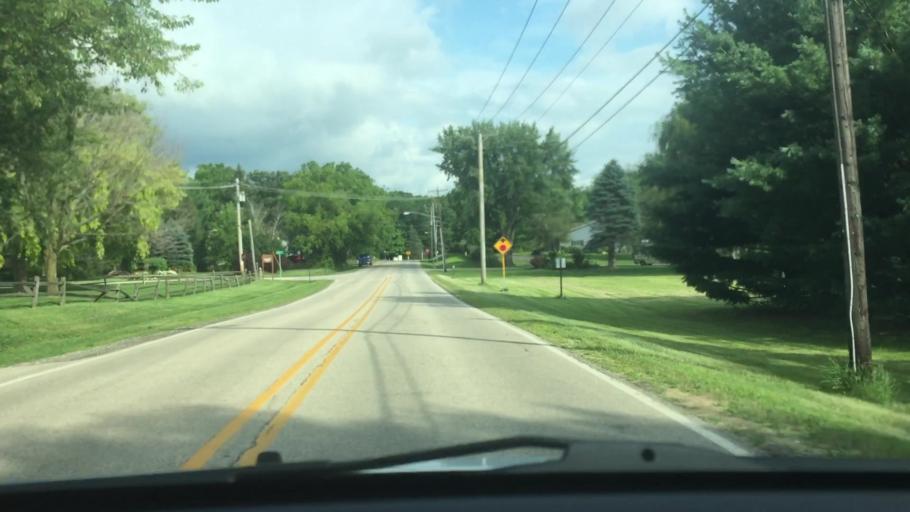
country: US
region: Illinois
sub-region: McHenry County
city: Crystal Lake
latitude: 42.2640
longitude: -88.3376
